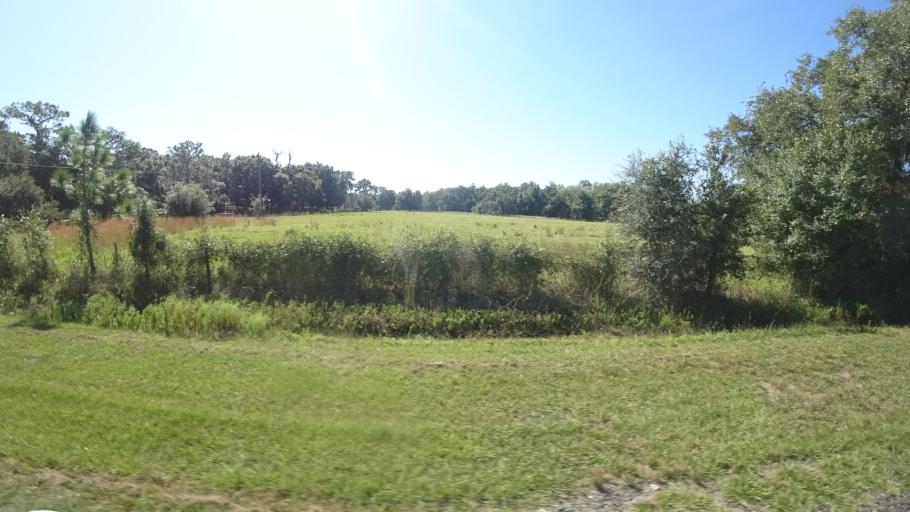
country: US
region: Florida
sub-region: Sarasota County
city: Warm Mineral Springs
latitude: 27.2736
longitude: -82.1592
